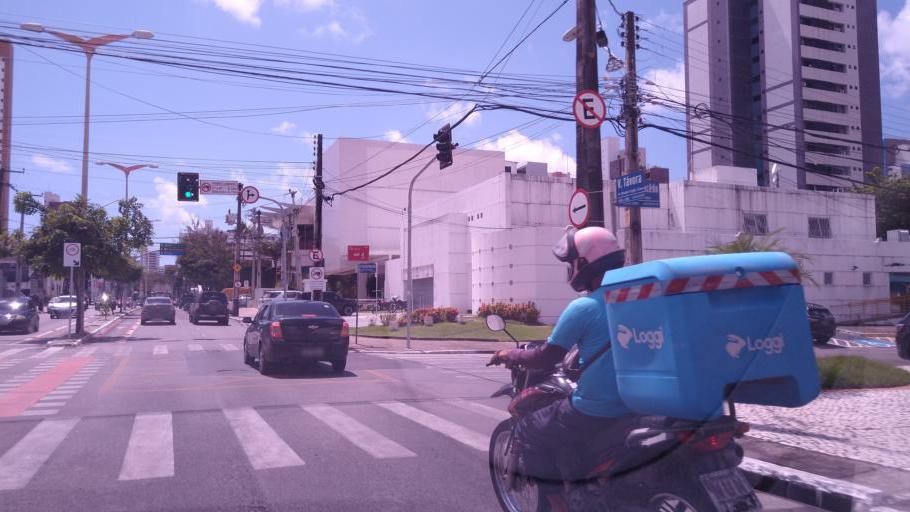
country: BR
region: Ceara
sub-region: Fortaleza
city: Fortaleza
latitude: -3.7360
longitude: -38.4928
